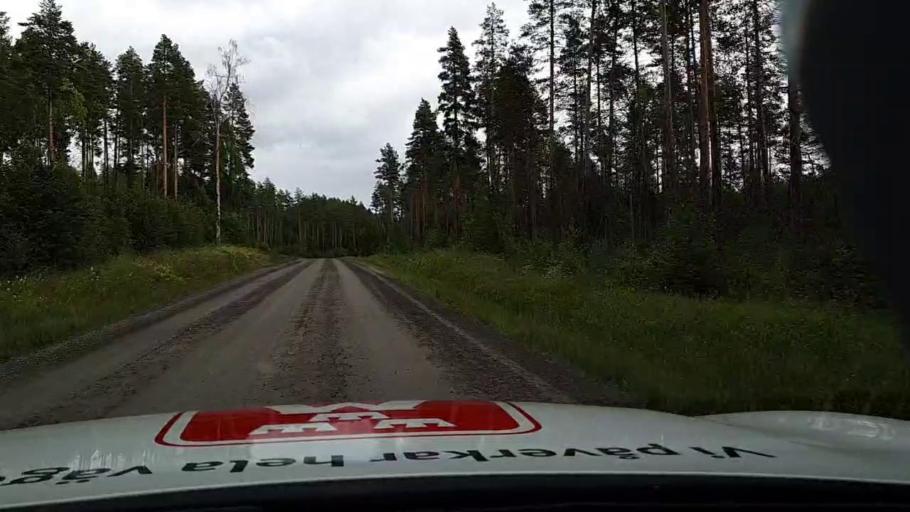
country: SE
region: Vaesternorrland
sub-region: Solleftea Kommun
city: As
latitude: 63.5115
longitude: 16.3956
